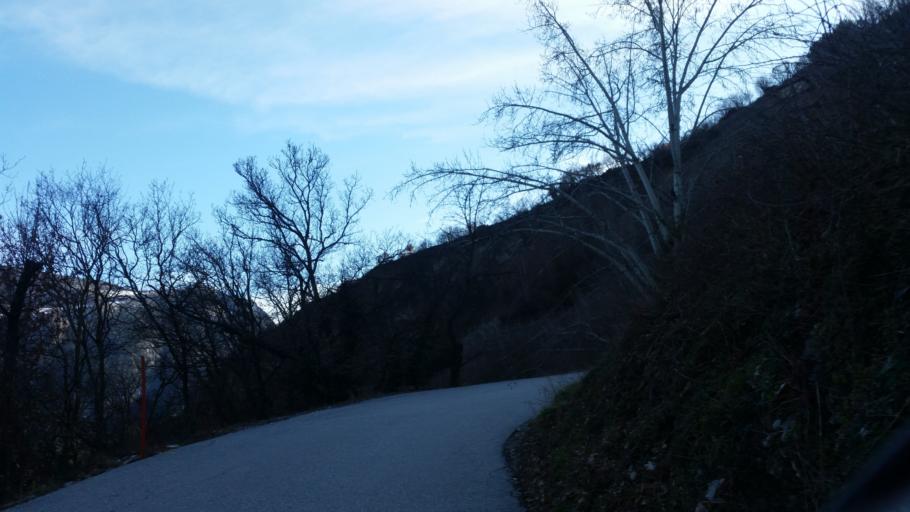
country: CH
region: Valais
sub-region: Sion District
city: Saint-Leonard
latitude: 46.2618
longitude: 7.4097
